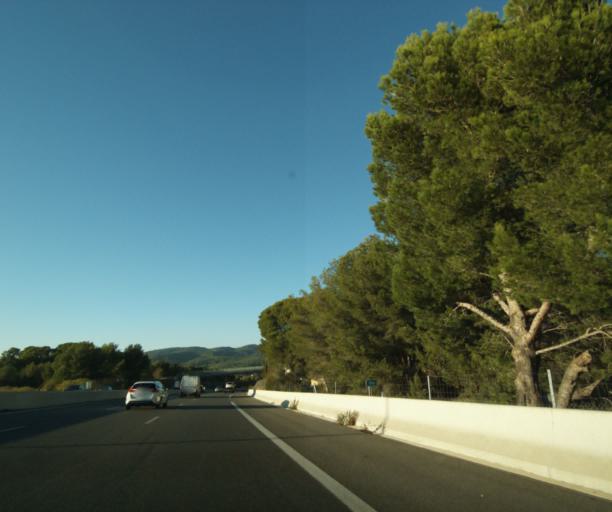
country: FR
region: Provence-Alpes-Cote d'Azur
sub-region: Departement des Bouches-du-Rhone
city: Ceyreste
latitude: 43.2013
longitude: 5.6339
